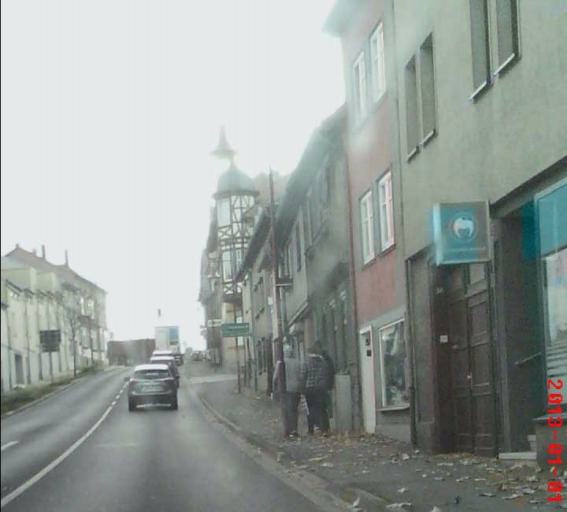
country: DE
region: Thuringia
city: Muehlhausen
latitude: 51.2114
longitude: 10.4492
